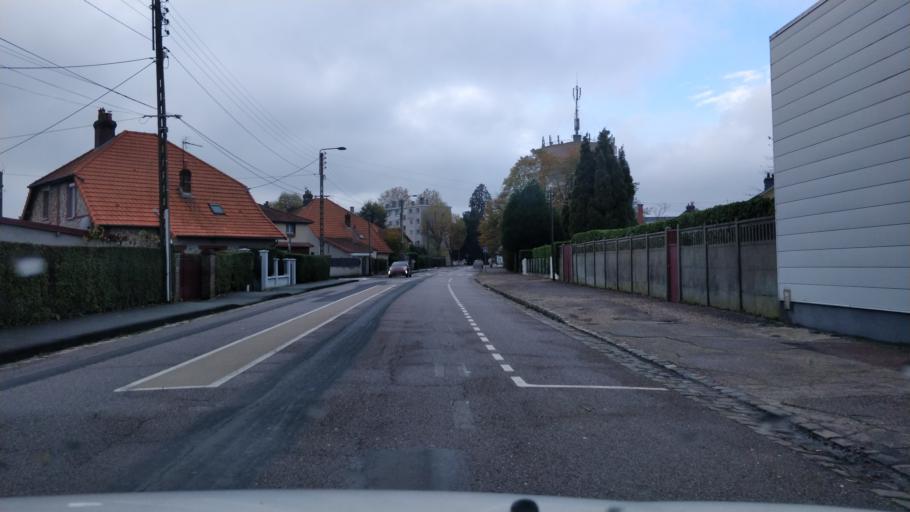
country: FR
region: Haute-Normandie
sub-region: Departement de la Seine-Maritime
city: Bihorel
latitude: 49.4546
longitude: 1.1241
